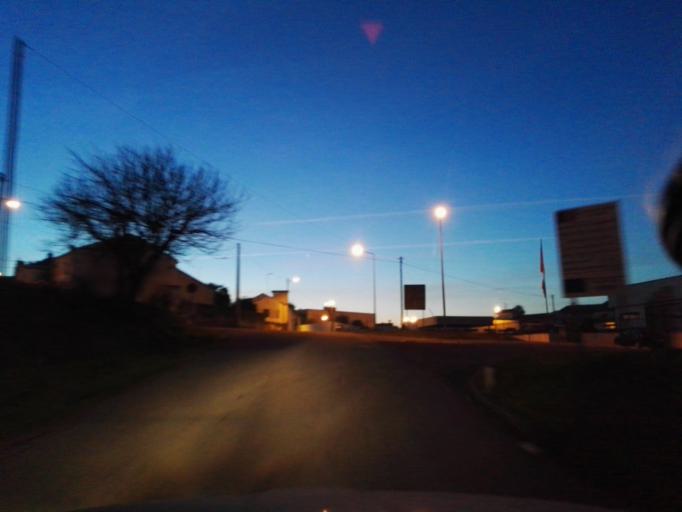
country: PT
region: Evora
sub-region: Arraiolos
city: Arraiolos
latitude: 38.8321
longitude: -7.8358
